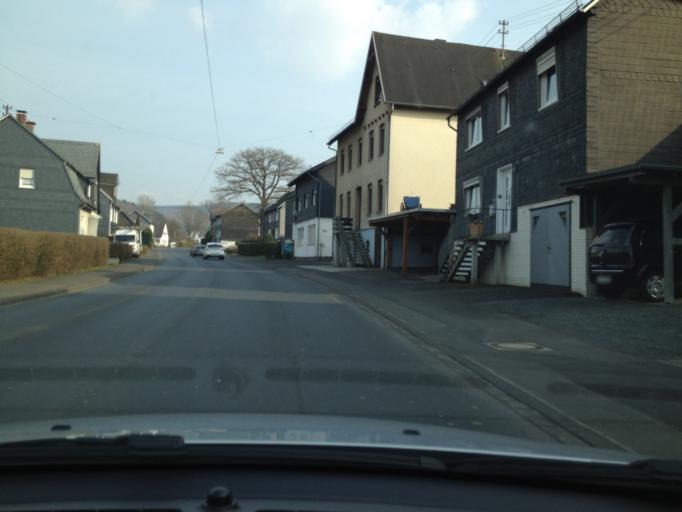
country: DE
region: North Rhine-Westphalia
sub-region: Regierungsbezirk Arnsberg
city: Neunkirchen
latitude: 50.7815
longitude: 8.0323
